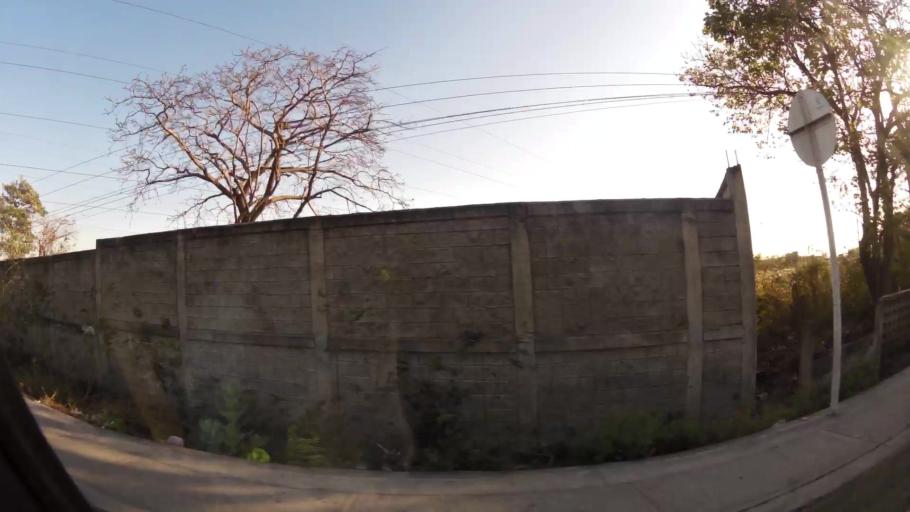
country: CO
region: Atlantico
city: Soledad
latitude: 10.9321
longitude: -74.7822
